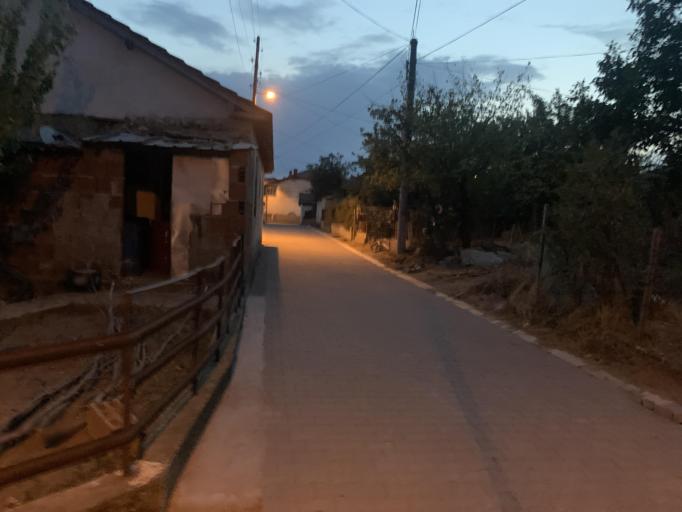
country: MK
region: Bogdanci
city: Bogdanci
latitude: 41.2007
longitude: 22.5748
